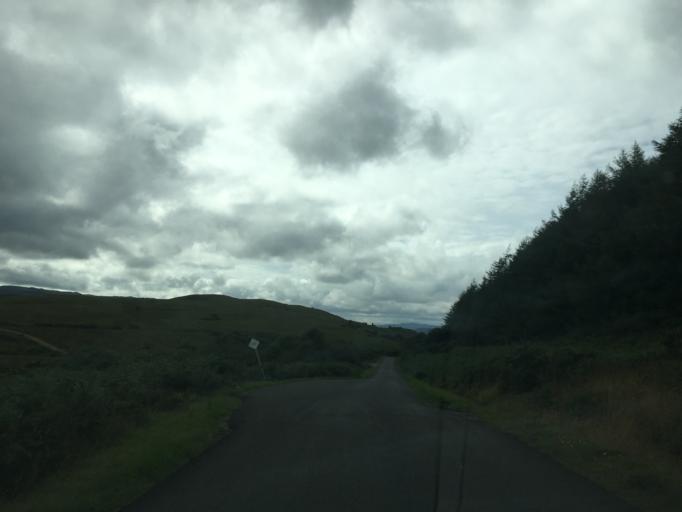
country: GB
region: Scotland
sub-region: Argyll and Bute
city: Tarbert
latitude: 55.8711
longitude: -5.2885
